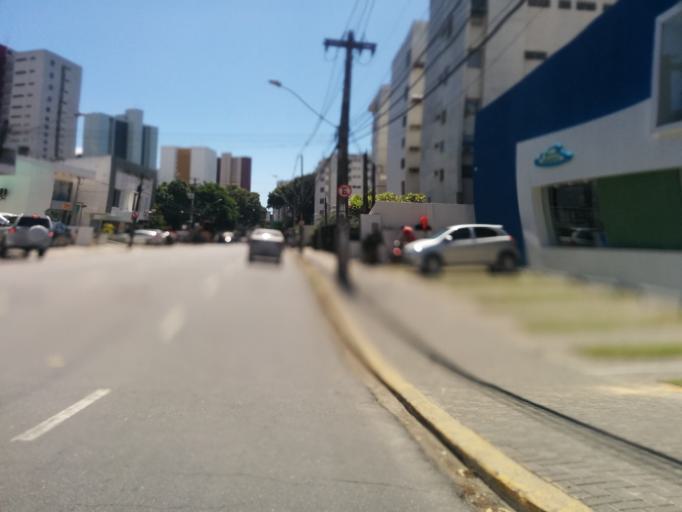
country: BR
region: Pernambuco
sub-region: Recife
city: Recife
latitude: -8.0455
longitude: -34.8970
